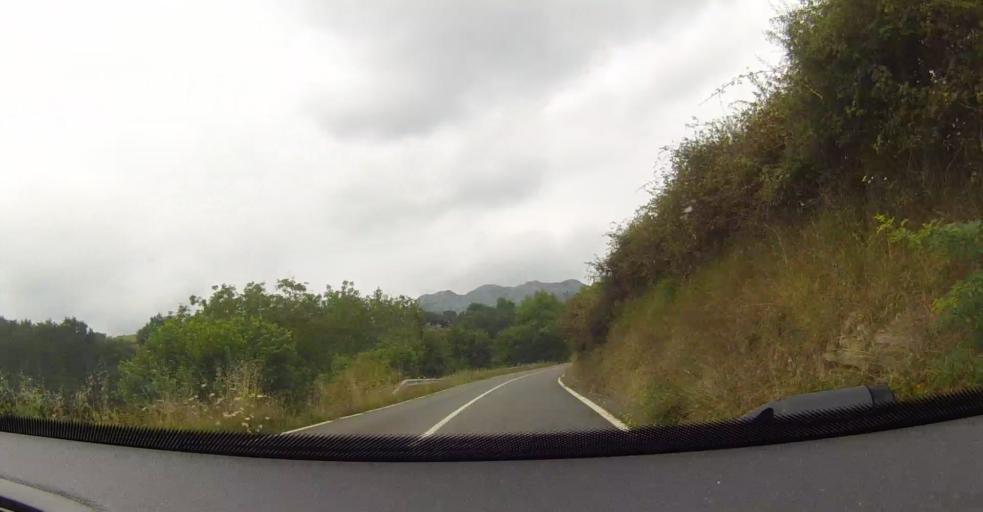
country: ES
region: Cantabria
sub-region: Provincia de Cantabria
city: Rasines
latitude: 43.2551
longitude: -3.3660
